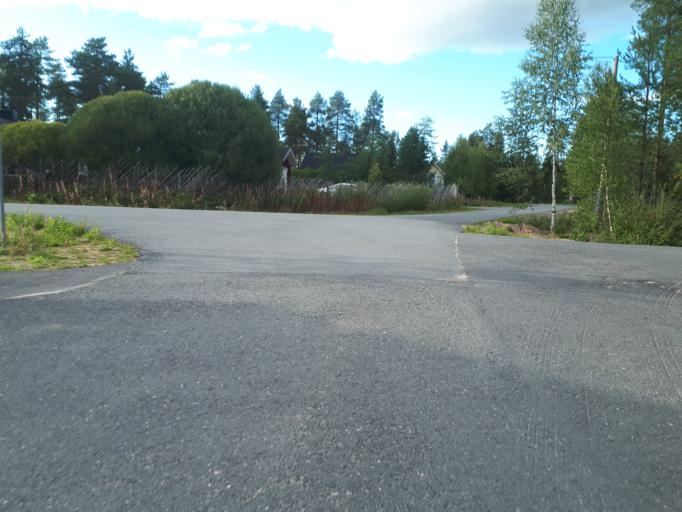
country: FI
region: Northern Ostrobothnia
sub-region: Oulunkaari
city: Ii
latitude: 65.3250
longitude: 25.4185
